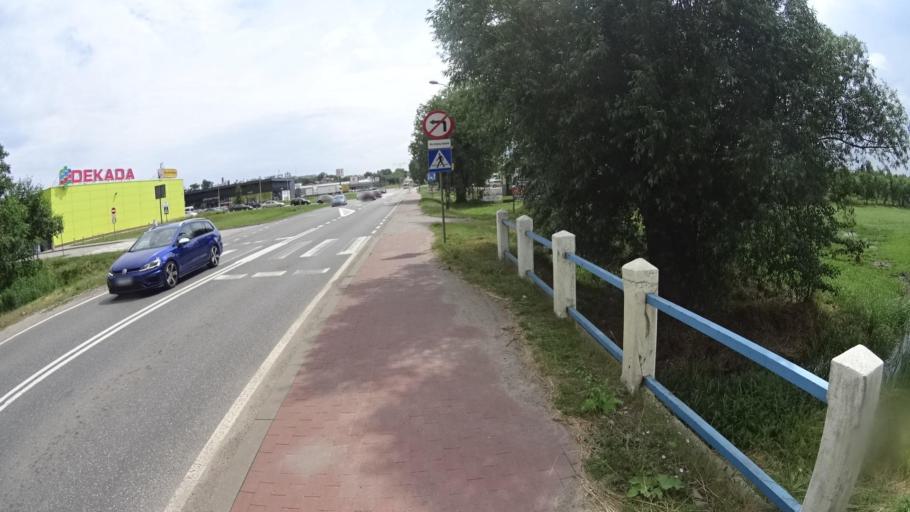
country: PL
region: Masovian Voivodeship
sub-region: Powiat grojecki
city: Grojec
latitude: 51.8748
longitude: 20.8644
